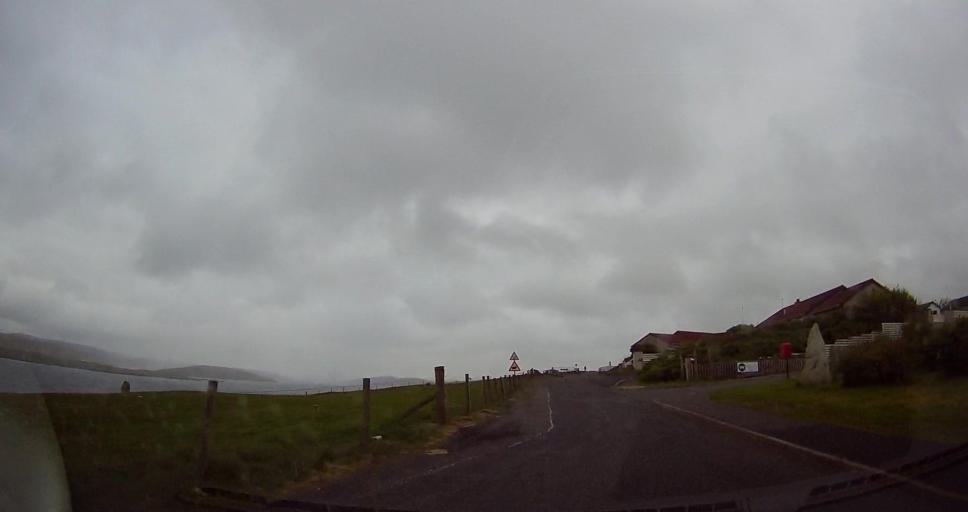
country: GB
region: Scotland
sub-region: Shetland Islands
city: Lerwick
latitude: 60.3901
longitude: -1.3696
